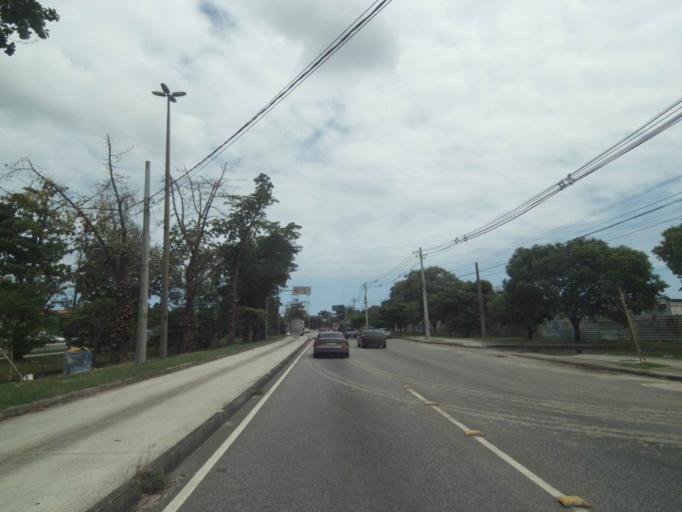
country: BR
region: Rio de Janeiro
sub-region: Sao Joao De Meriti
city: Sao Joao de Meriti
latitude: -22.9433
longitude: -43.3726
